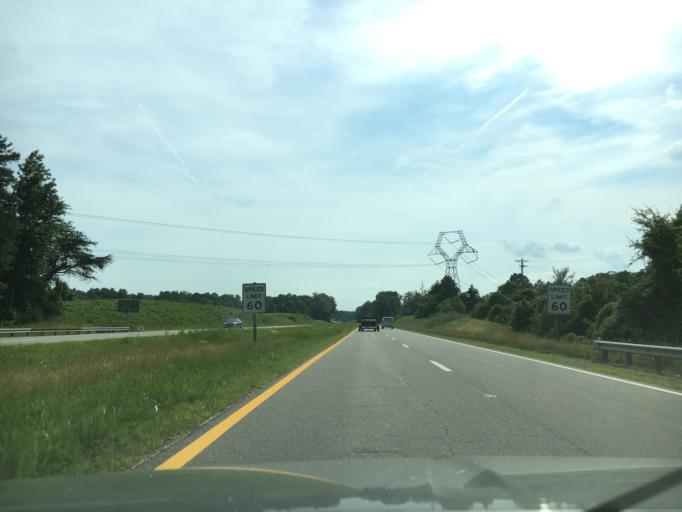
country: US
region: Virginia
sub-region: Mecklenburg County
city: Chase City
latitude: 36.8644
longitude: -78.5870
